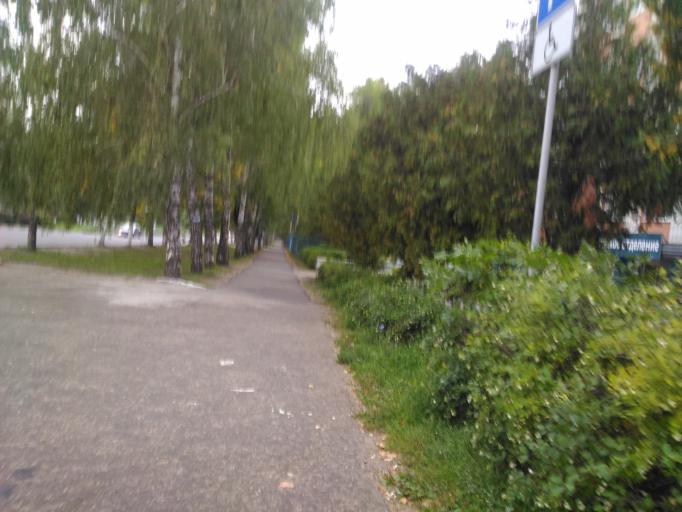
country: RU
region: Ulyanovsk
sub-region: Ulyanovskiy Rayon
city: Ulyanovsk
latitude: 54.2659
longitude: 48.3347
